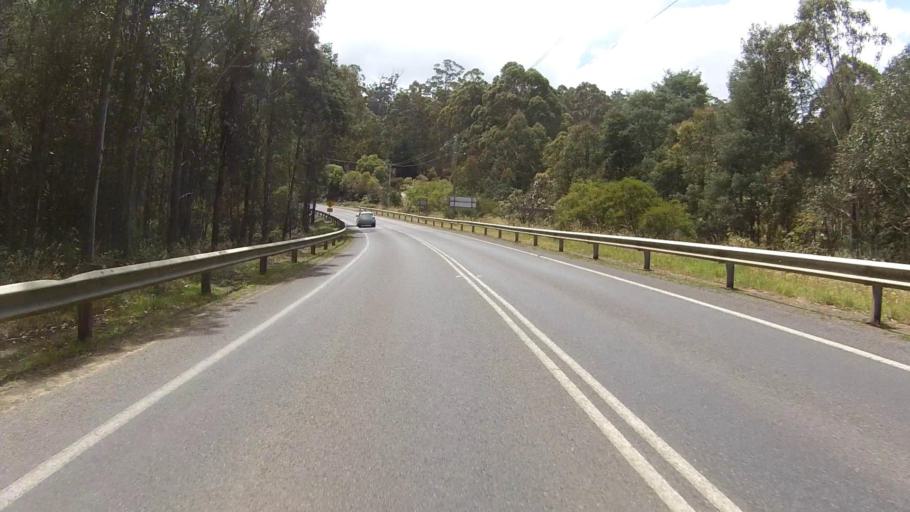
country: AU
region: Tasmania
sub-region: Kingborough
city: Kettering
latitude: -43.1055
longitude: 147.2452
